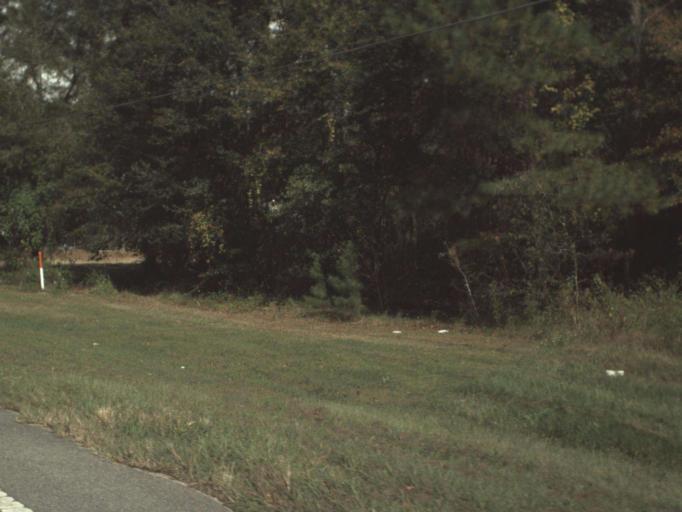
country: US
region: Florida
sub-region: Gadsden County
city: Gretna
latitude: 30.6792
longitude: -84.6186
